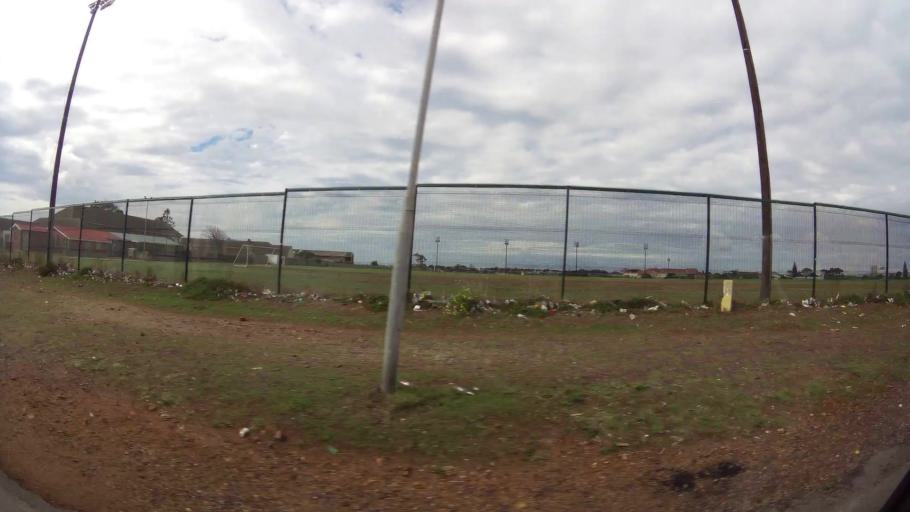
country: ZA
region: Eastern Cape
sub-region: Nelson Mandela Bay Metropolitan Municipality
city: Port Elizabeth
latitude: -33.9376
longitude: 25.5692
